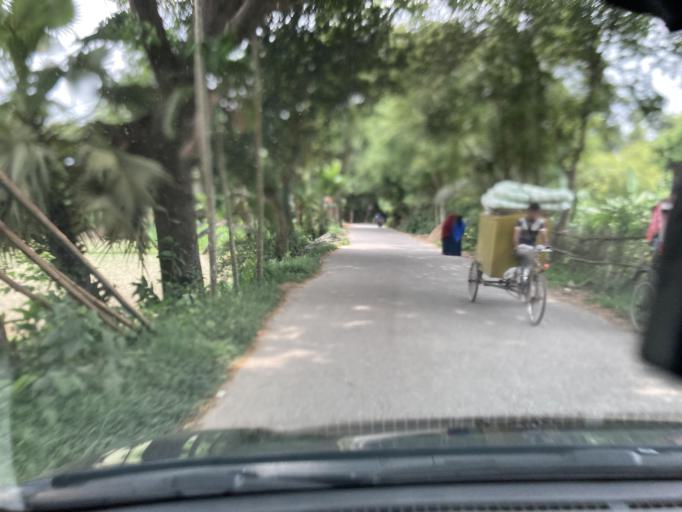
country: BD
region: Dhaka
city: Dohar
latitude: 23.8129
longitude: 90.0468
